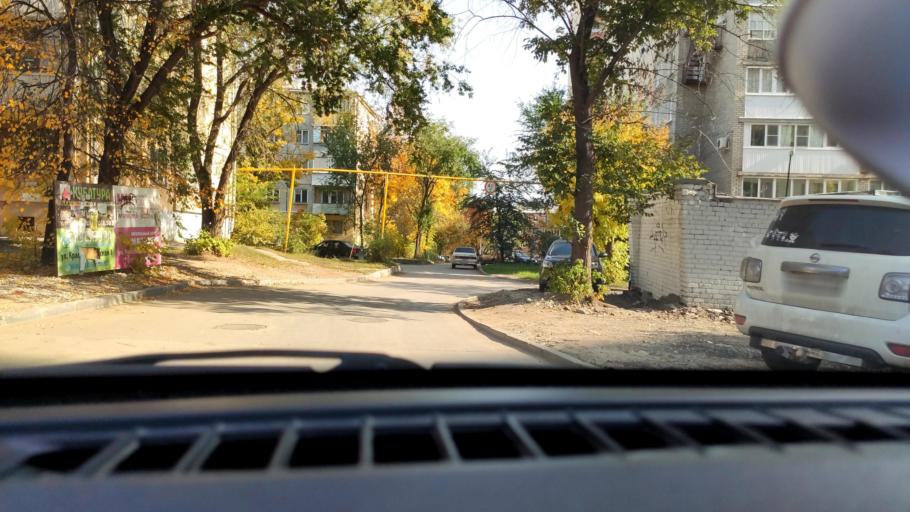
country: RU
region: Samara
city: Samara
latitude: 53.1950
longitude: 50.2064
